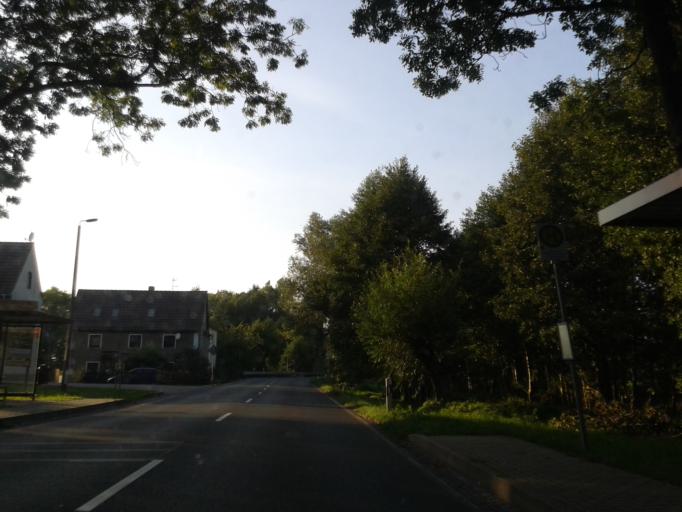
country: DE
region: Saxony
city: Klipphausen
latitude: 51.1079
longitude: 13.4862
